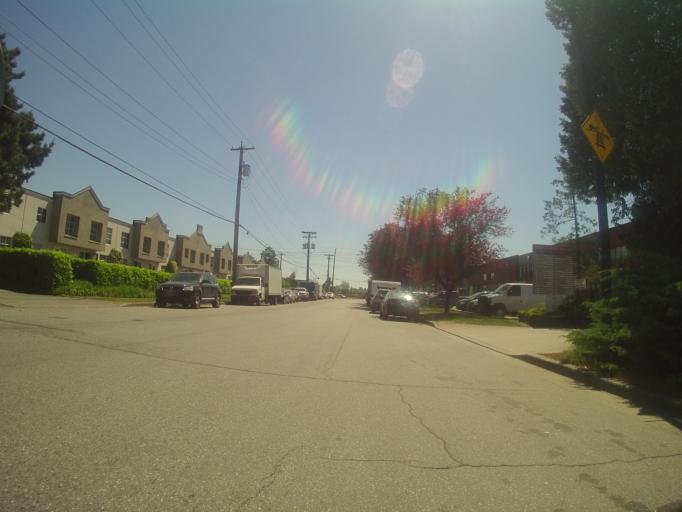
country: CA
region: British Columbia
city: Vancouver
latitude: 49.2080
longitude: -123.1069
